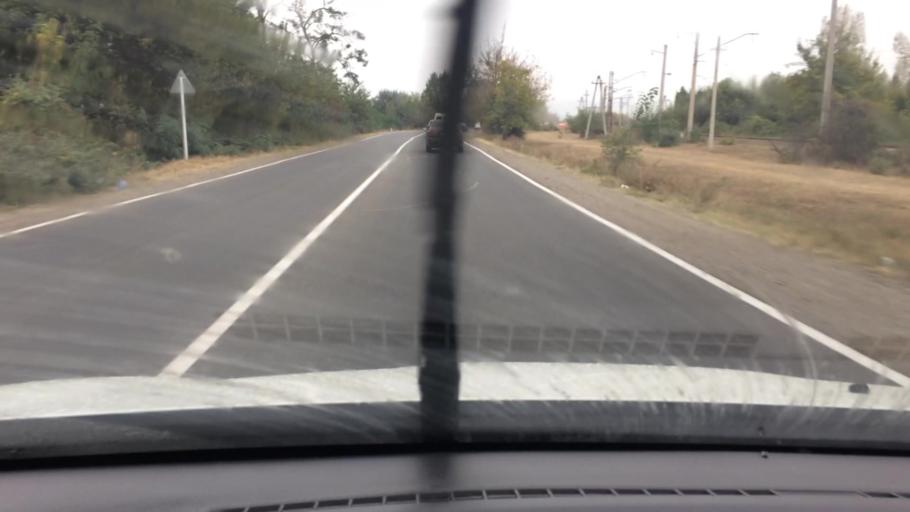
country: GE
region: Kvemo Kartli
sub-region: Marneuli
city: Marneuli
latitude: 41.4147
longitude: 44.8276
